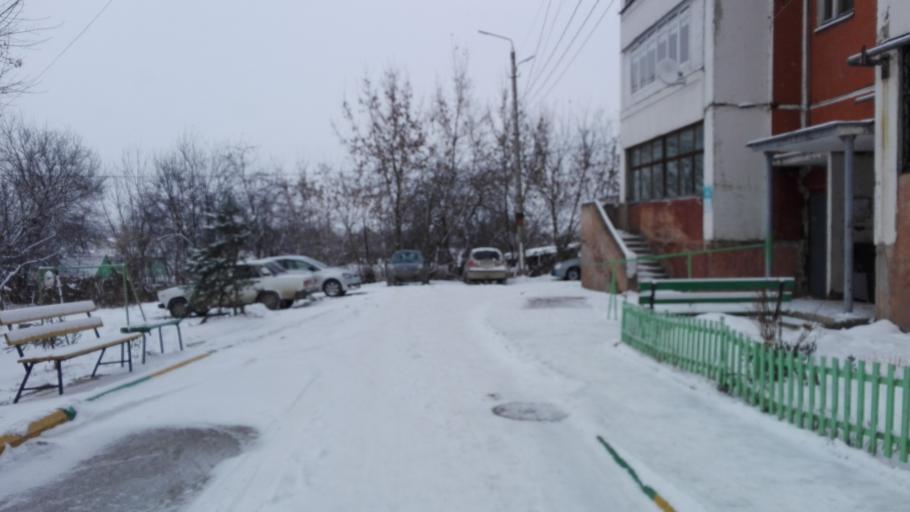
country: RU
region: Tula
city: Kosaya Gora
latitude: 54.1210
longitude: 37.5384
